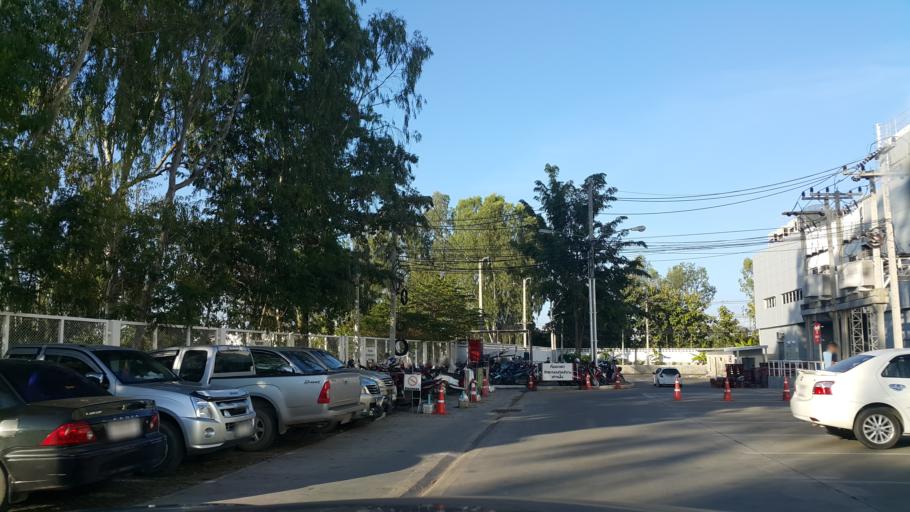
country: TH
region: Lamphun
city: Lamphun
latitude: 18.5912
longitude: 99.0402
